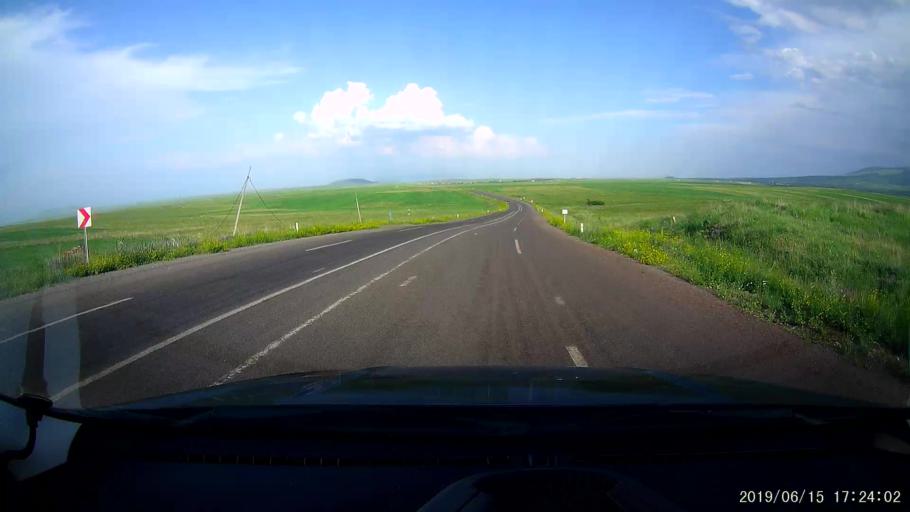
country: TR
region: Kars
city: Basgedikler
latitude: 40.6160
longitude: 43.3754
